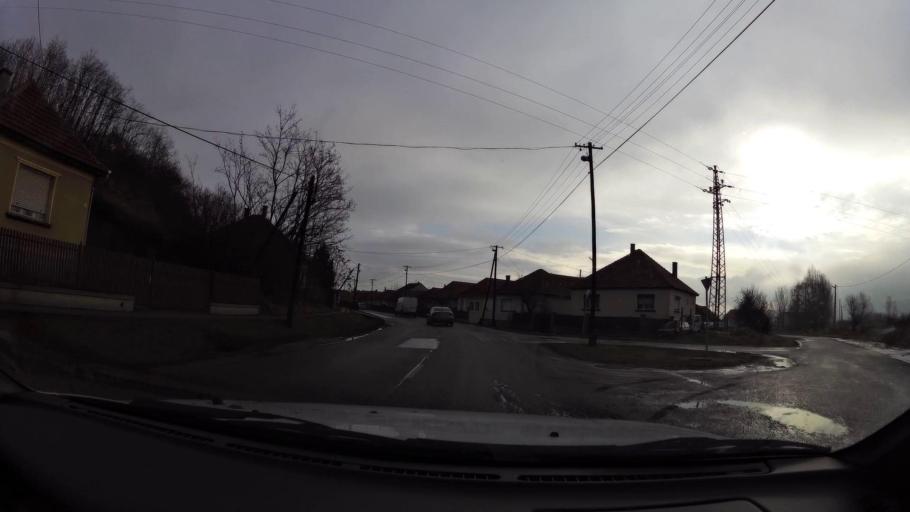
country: HU
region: Borsod-Abauj-Zemplen
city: Mucsony
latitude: 48.2744
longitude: 20.6677
